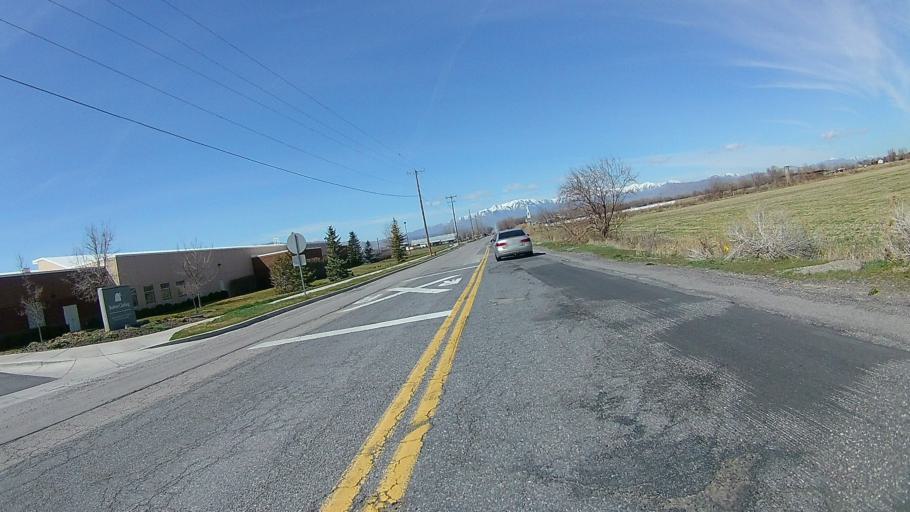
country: US
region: Utah
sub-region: Utah County
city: American Fork
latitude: 40.3552
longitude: -111.7877
